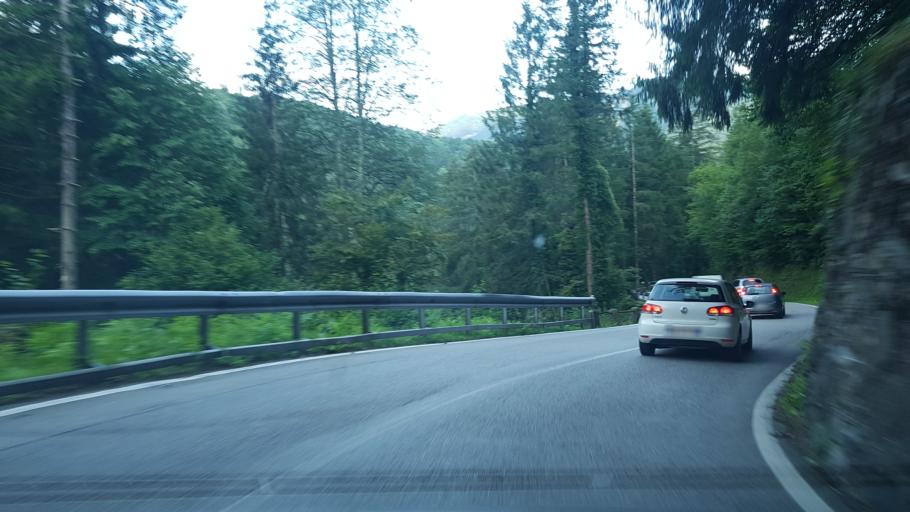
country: IT
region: Friuli Venezia Giulia
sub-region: Provincia di Udine
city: Comeglians
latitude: 46.5333
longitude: 12.8669
